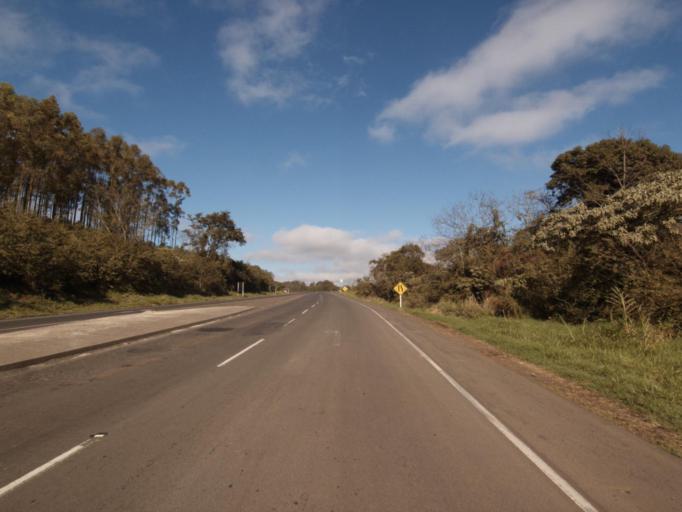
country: BR
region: Rio Grande do Sul
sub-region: Frederico Westphalen
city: Frederico Westphalen
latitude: -27.0710
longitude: -53.2305
